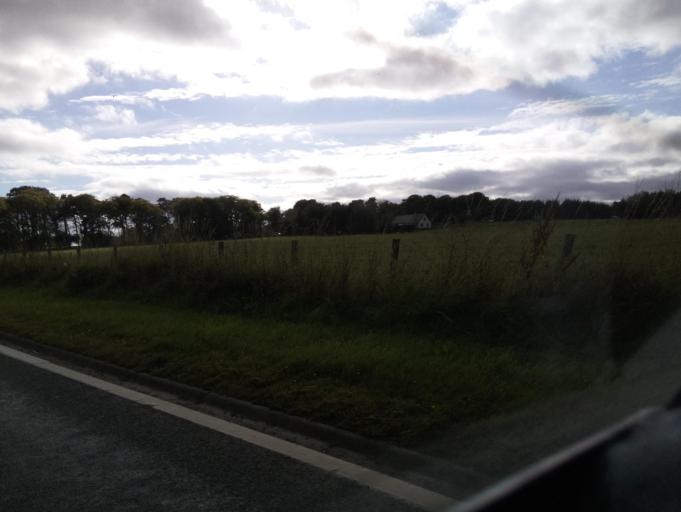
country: GB
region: Scotland
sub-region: The Scottish Borders
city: West Linton
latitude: 55.7782
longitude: -3.3422
